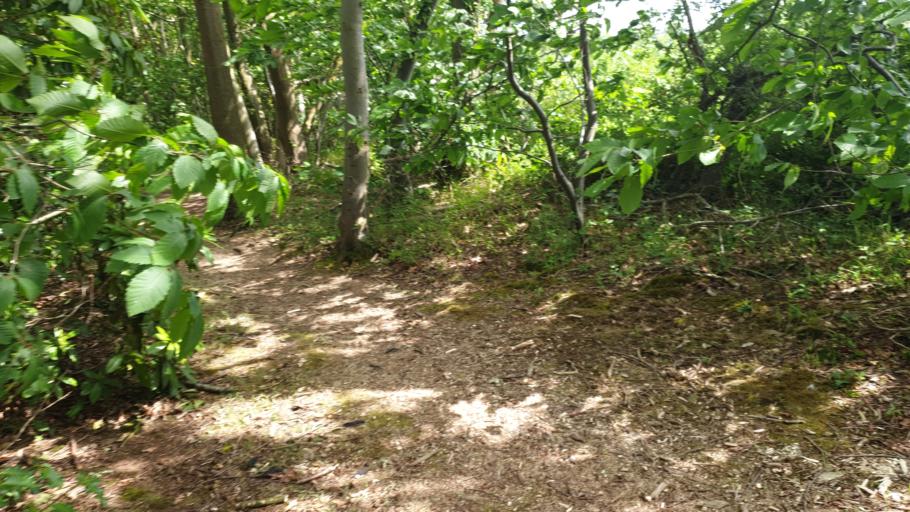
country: GB
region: England
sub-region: Essex
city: Great Bentley
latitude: 51.8790
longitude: 1.0779
